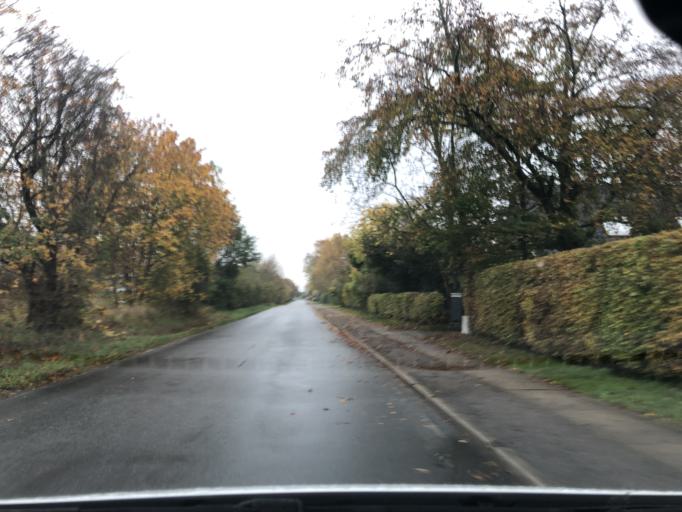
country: DK
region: Capital Region
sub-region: Tarnby Kommune
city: Tarnby
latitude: 55.5689
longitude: 12.6078
